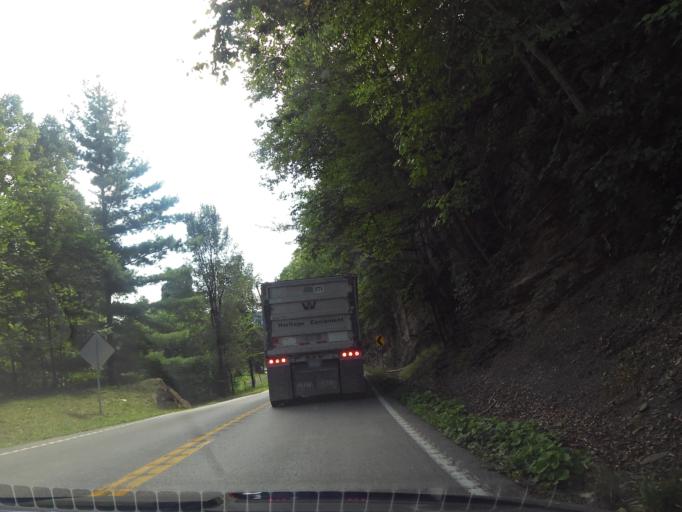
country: US
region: Kentucky
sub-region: Harlan County
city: Harlan
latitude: 36.8889
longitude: -83.3100
